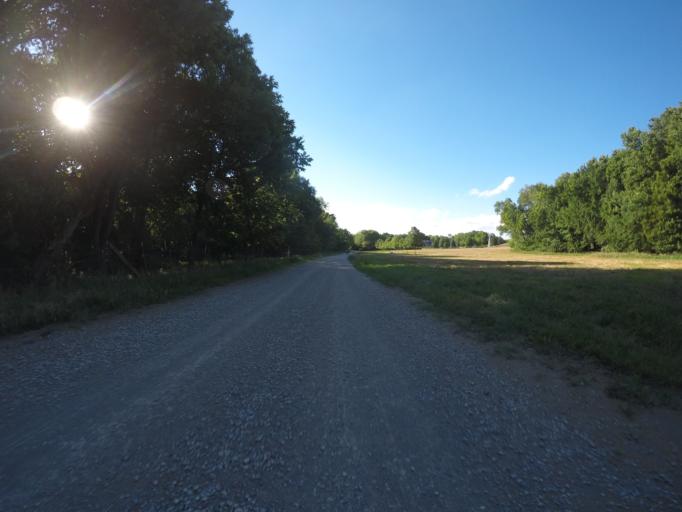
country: US
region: Kansas
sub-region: Riley County
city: Ogden
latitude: 39.2471
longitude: -96.7358
